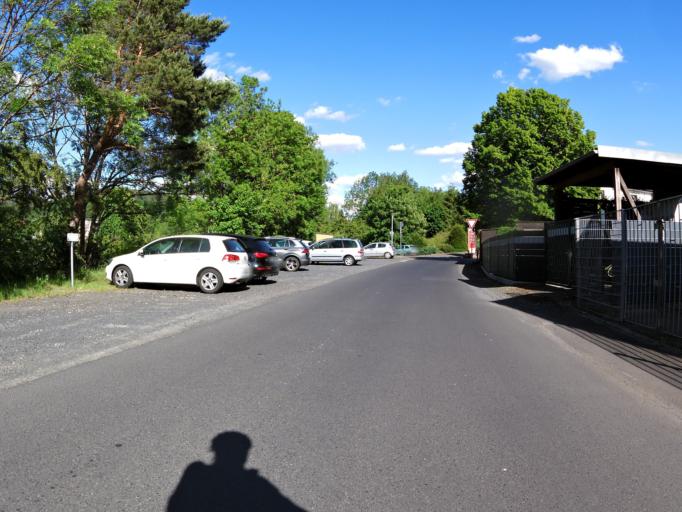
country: DE
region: Hesse
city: Philippsthal
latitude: 50.8402
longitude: 9.9969
